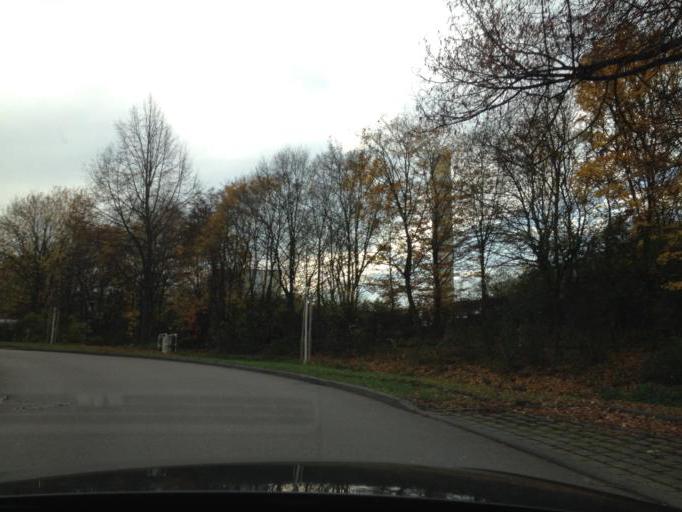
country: DE
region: Baden-Wuerttemberg
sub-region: Regierungsbezirk Stuttgart
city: Neckarsulm
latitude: 49.2132
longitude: 9.2384
